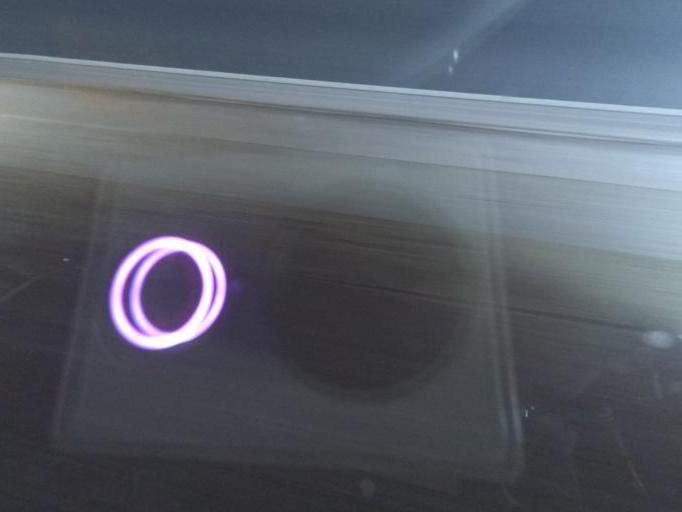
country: DK
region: Central Jutland
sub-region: Skanderborg Kommune
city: Horning
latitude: 56.0994
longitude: 10.0309
